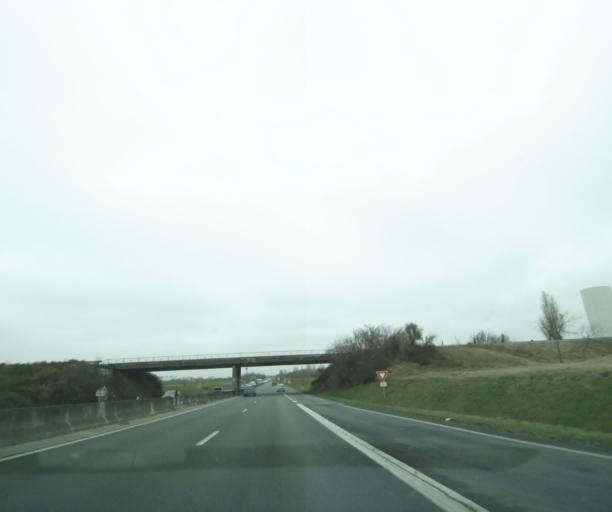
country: FR
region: Poitou-Charentes
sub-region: Departement de la Charente-Maritime
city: Aytre
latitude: 46.1420
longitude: -1.1065
